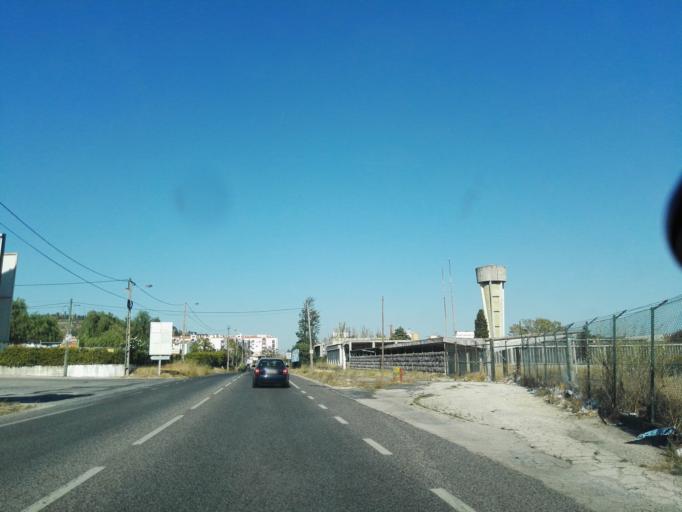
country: PT
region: Lisbon
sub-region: Vila Franca de Xira
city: Sobralinho
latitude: 38.9112
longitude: -9.0254
